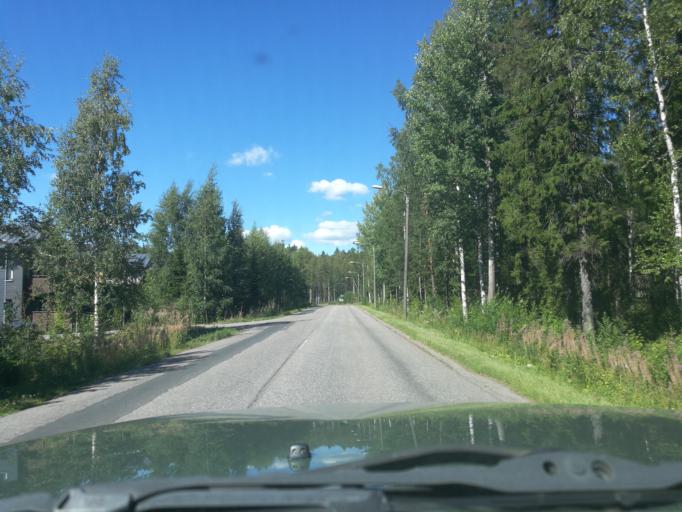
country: FI
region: Uusimaa
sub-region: Helsinki
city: Kerava
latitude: 60.3583
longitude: 25.1065
